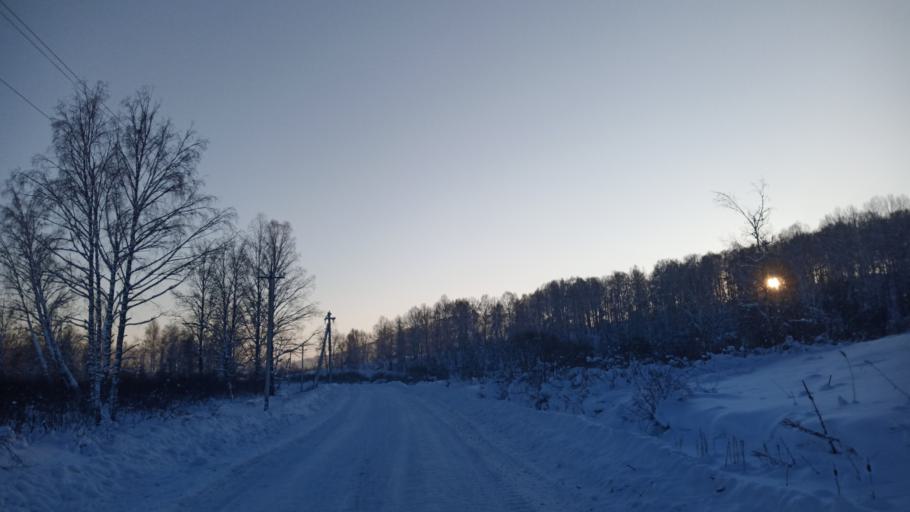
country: RU
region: Altai Krai
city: Krasnogorskoye
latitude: 52.1262
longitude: 86.2046
